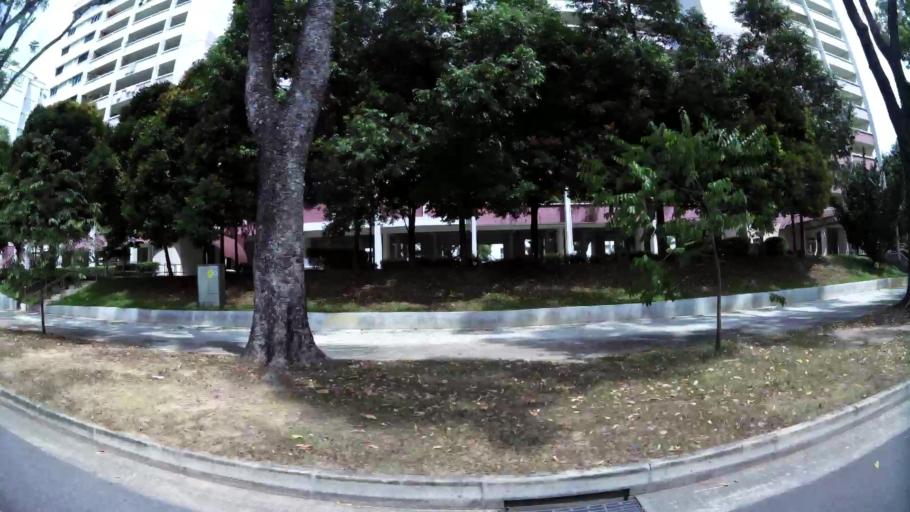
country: MY
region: Johor
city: Johor Bahru
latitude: 1.3465
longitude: 103.7252
